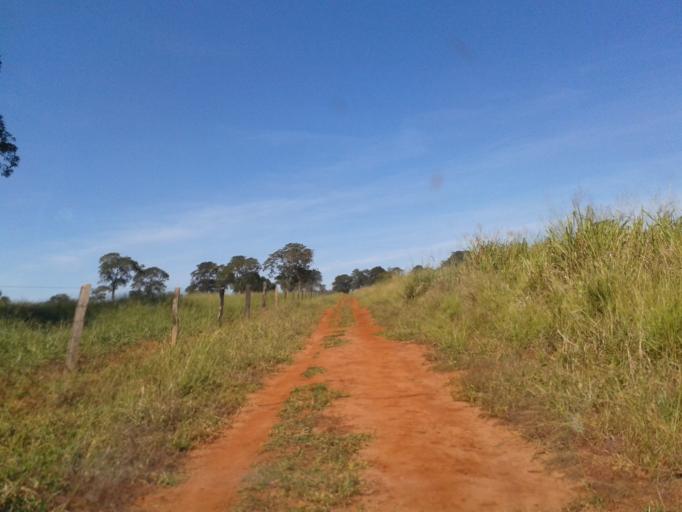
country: BR
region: Minas Gerais
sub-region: Santa Vitoria
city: Santa Vitoria
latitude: -19.0057
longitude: -50.3181
